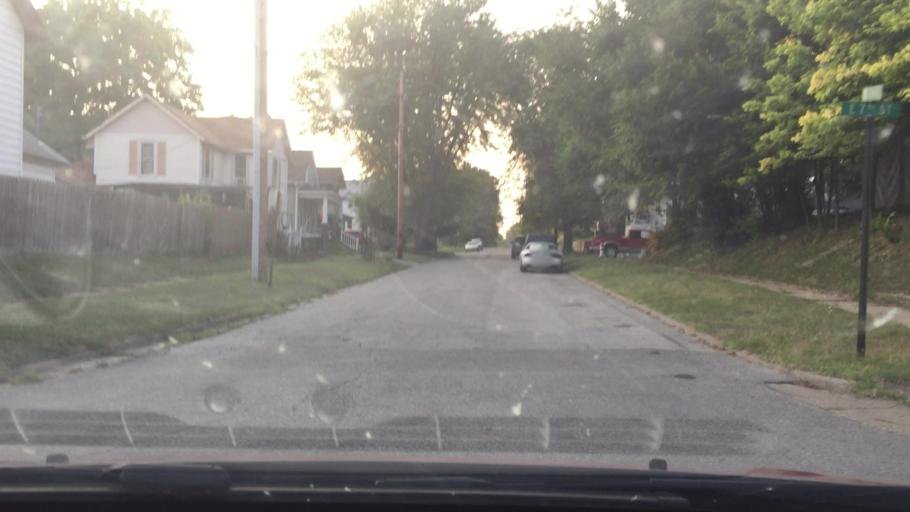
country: US
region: Iowa
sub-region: Muscatine County
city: Muscatine
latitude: 41.4283
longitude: -91.0443
